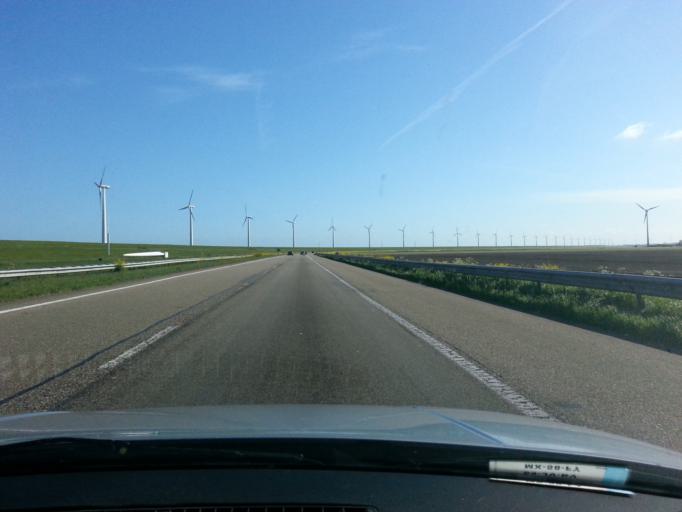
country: NL
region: Flevoland
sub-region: Gemeente Urk
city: Urk
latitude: 52.5863
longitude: 5.5527
